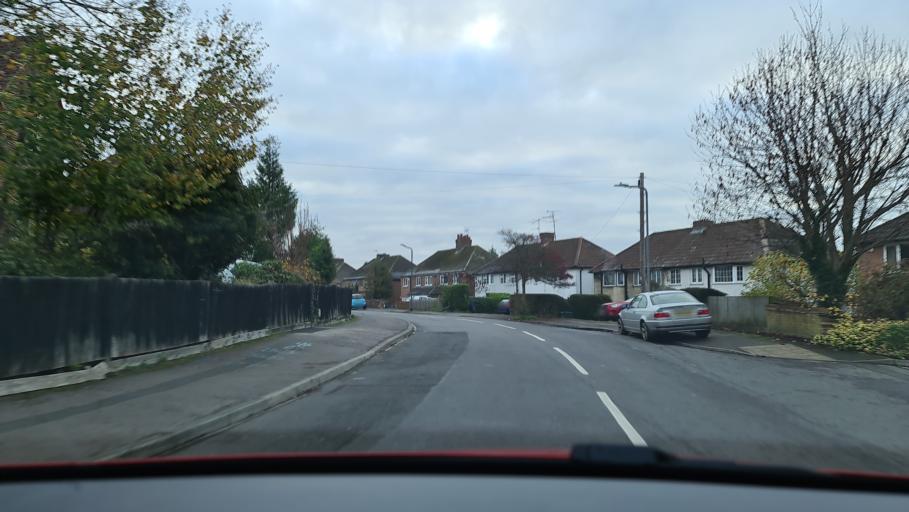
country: GB
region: England
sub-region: Buckinghamshire
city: High Wycombe
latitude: 51.6407
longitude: -0.7787
